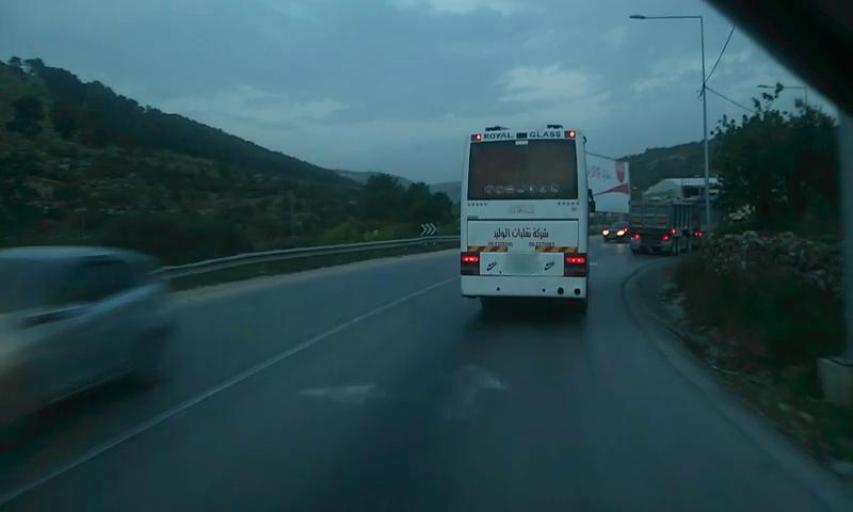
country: PS
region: West Bank
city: Kafr al Labad
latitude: 32.3171
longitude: 35.0917
